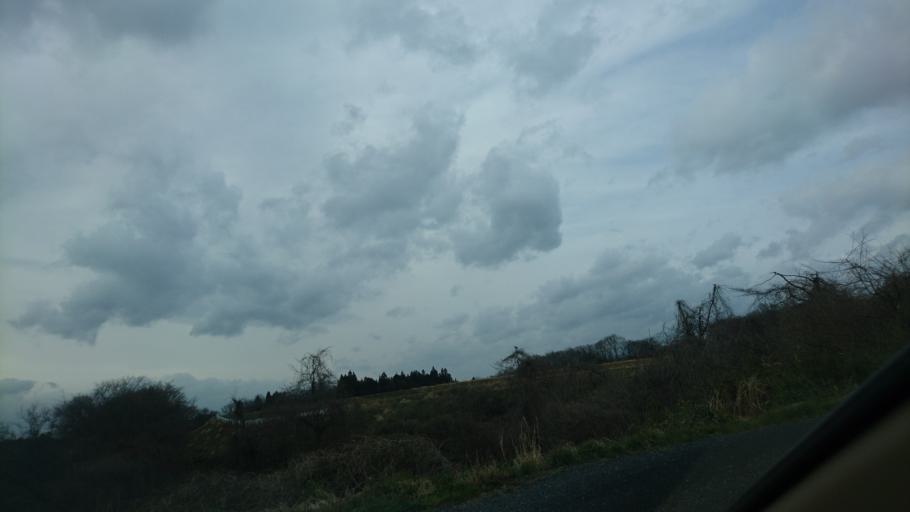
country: JP
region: Iwate
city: Ichinoseki
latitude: 38.8928
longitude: 141.1630
